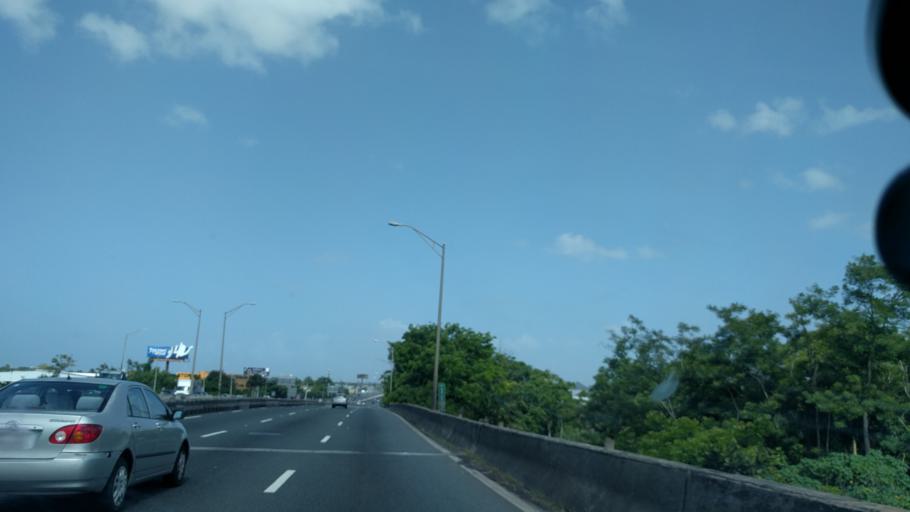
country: PR
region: Bayamon
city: Bayamon
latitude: 18.4220
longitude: -66.1548
